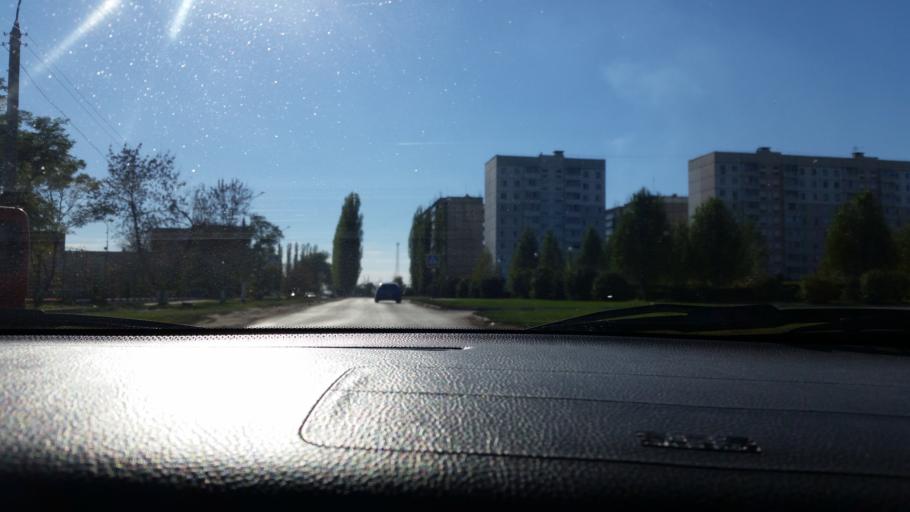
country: RU
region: Lipetsk
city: Gryazi
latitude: 52.4754
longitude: 39.9479
